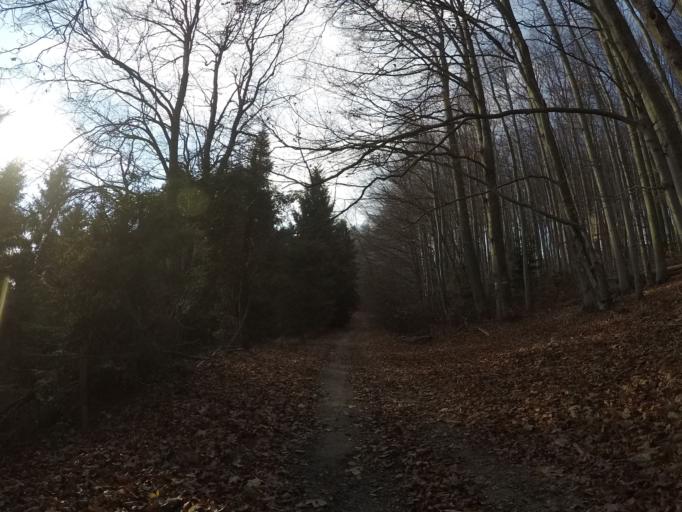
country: SK
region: Kosicky
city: Gelnica
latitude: 48.7650
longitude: 21.0565
